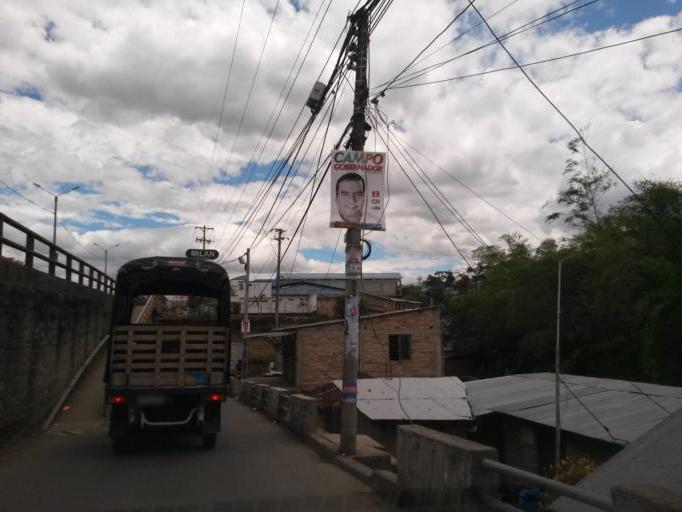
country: CO
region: Cauca
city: Popayan
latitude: 2.4812
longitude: -76.5700
